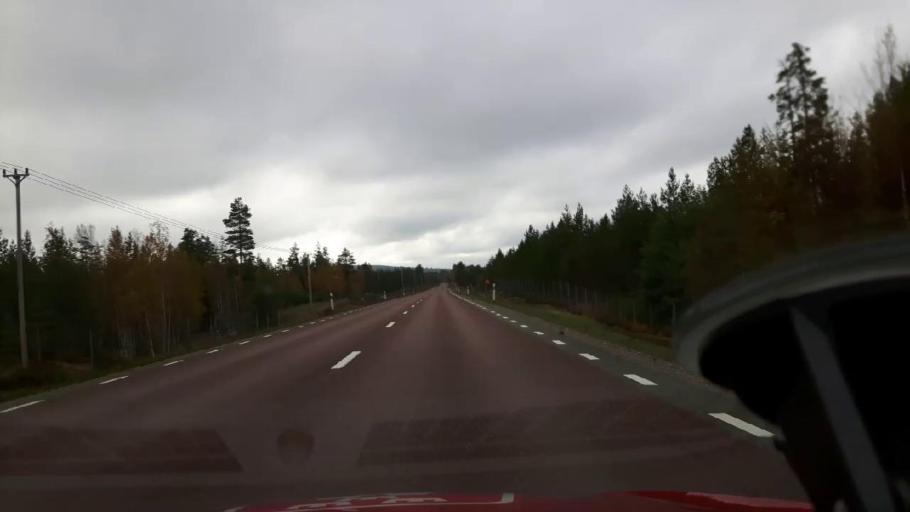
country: SE
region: Jaemtland
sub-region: Harjedalens Kommun
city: Sveg
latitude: 62.2306
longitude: 14.8413
